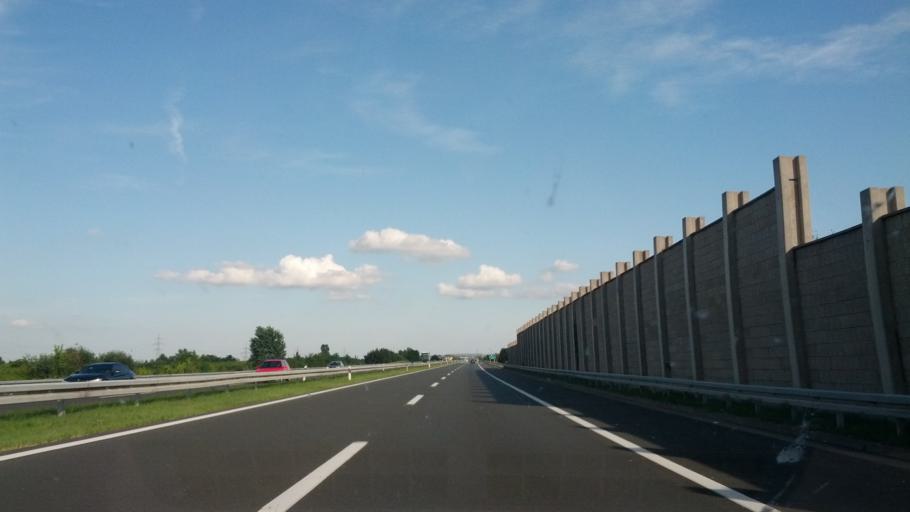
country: HR
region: Zagrebacka
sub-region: Grad Samobor
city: Samobor
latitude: 45.8129
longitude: 15.7637
